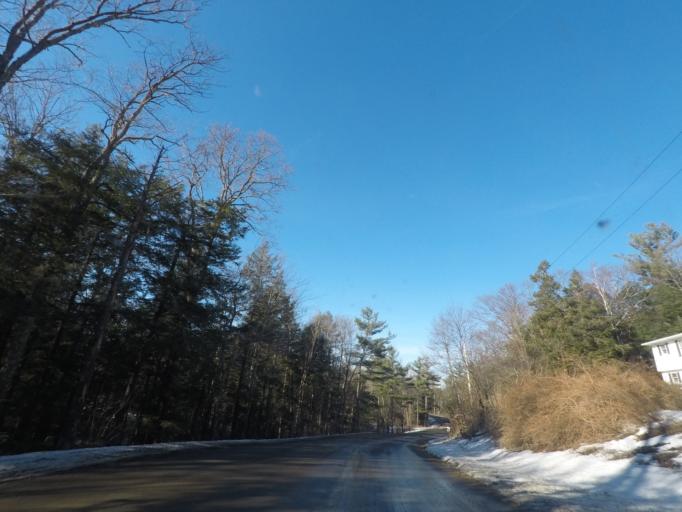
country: US
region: New York
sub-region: Rensselaer County
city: Averill Park
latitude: 42.6382
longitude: -73.5234
